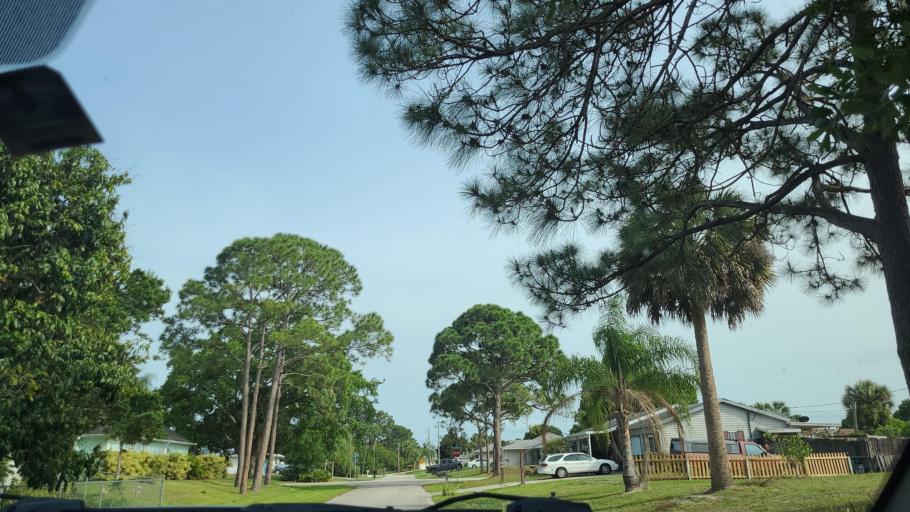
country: US
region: Florida
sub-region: Indian River County
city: Sebastian
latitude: 27.7614
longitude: -80.4789
